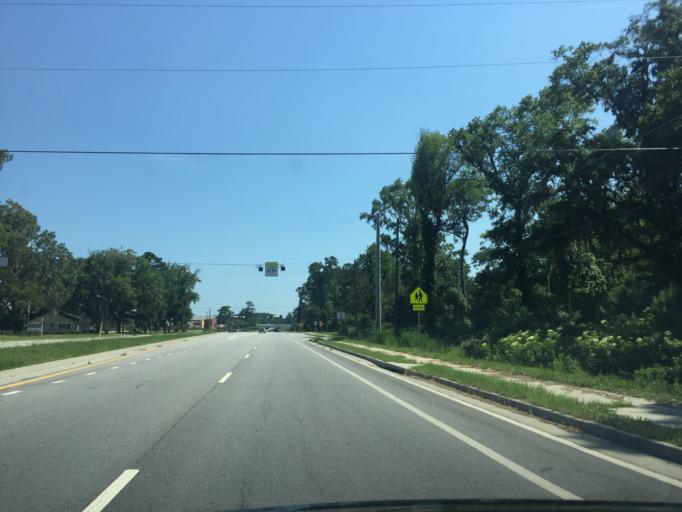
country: US
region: Georgia
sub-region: Chatham County
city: Montgomery
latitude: 31.9807
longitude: -81.1057
